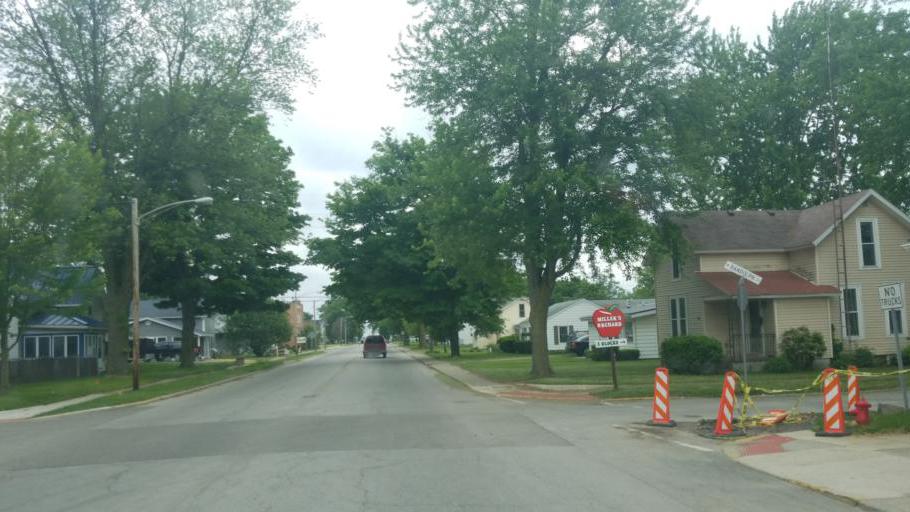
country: US
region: Indiana
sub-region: Elkhart County
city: Nappanee
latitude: 41.4399
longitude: -86.0014
